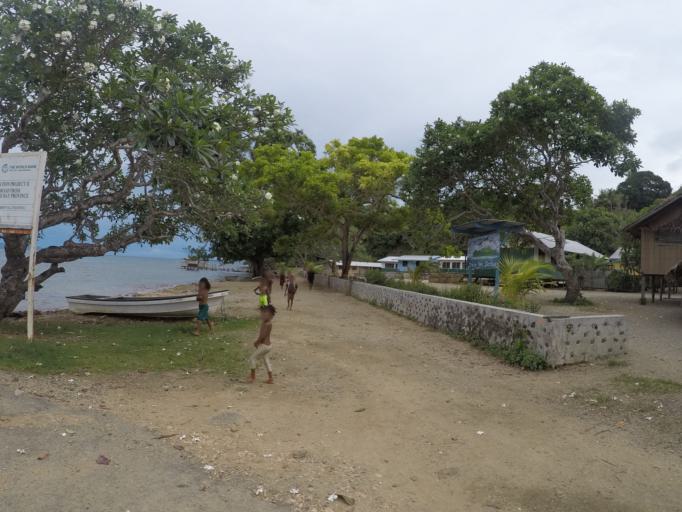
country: PG
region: Milne Bay
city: Alotau
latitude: -10.2260
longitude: 150.8749
